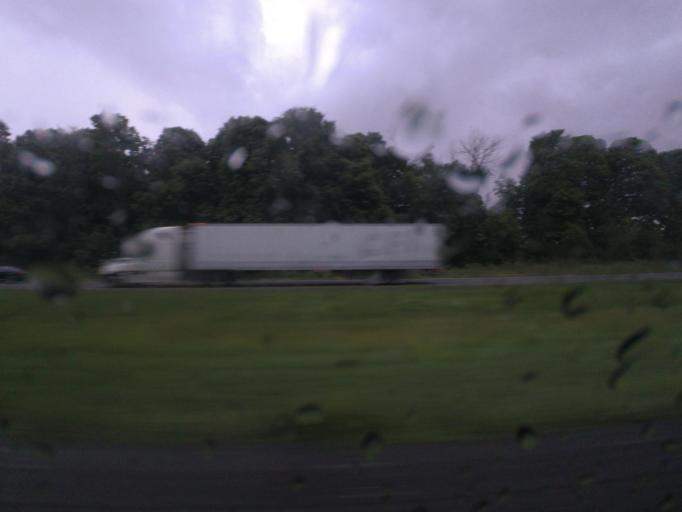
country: US
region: Indiana
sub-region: Wayne County
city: Cambridge City
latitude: 39.8542
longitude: -85.2154
